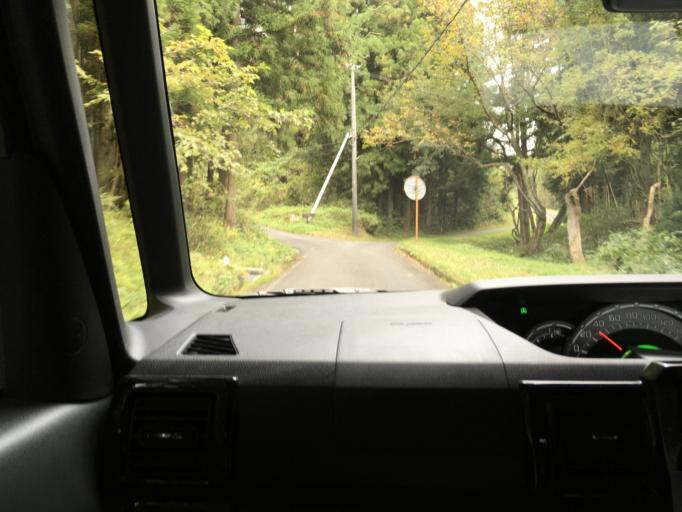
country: JP
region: Iwate
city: Mizusawa
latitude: 39.0262
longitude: 141.3557
